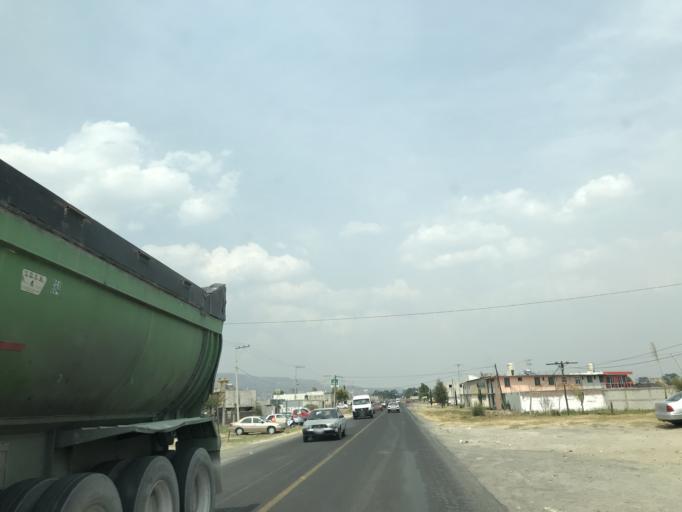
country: MX
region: Tlaxcala
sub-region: Ixtacuixtla de Mariano Matamoros
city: Santa Justina Ecatepec
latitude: 19.3125
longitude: -98.3401
